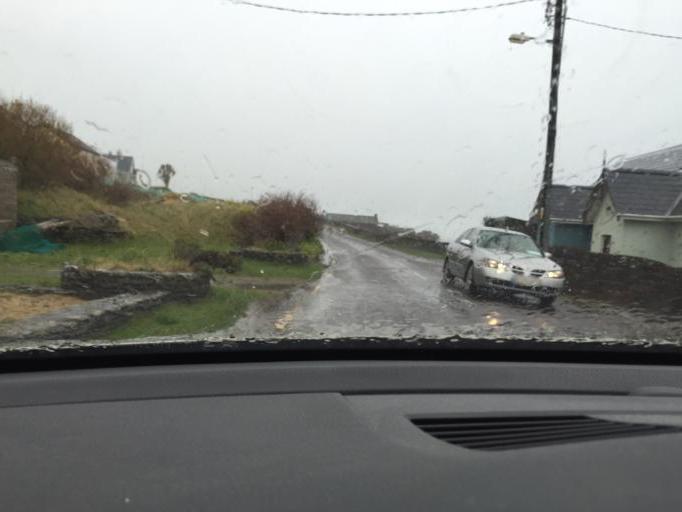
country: IE
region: Munster
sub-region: Ciarrai
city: Dingle
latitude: 52.1321
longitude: -10.3589
